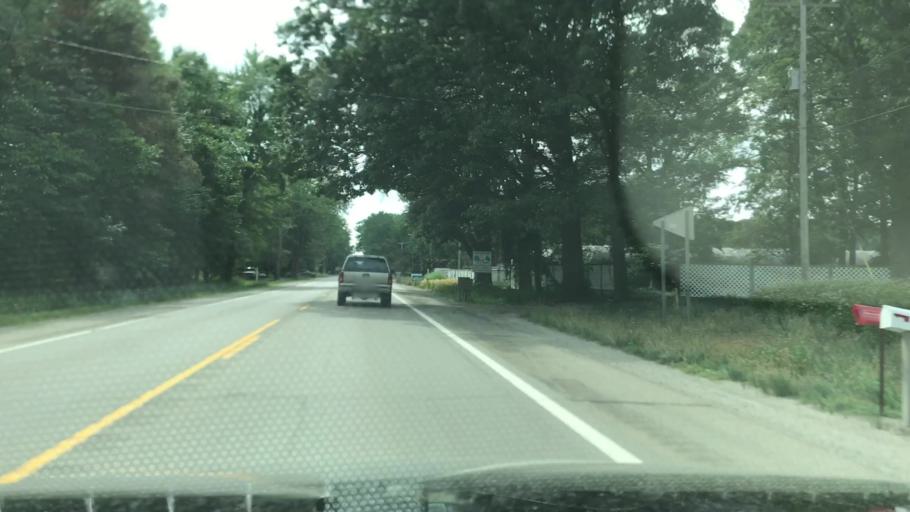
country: US
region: Michigan
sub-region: Ottawa County
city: Spring Lake
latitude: 43.0739
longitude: -86.1374
